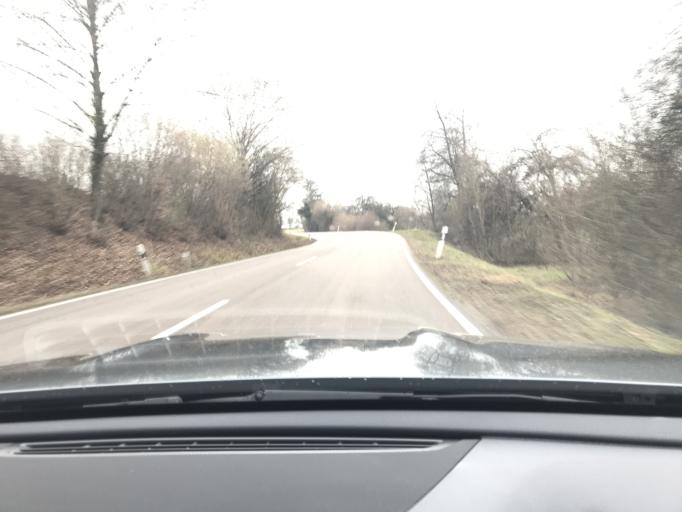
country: DE
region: Baden-Wuerttemberg
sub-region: Regierungsbezirk Stuttgart
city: Stuttgart Muehlhausen
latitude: 48.8852
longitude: 9.2595
